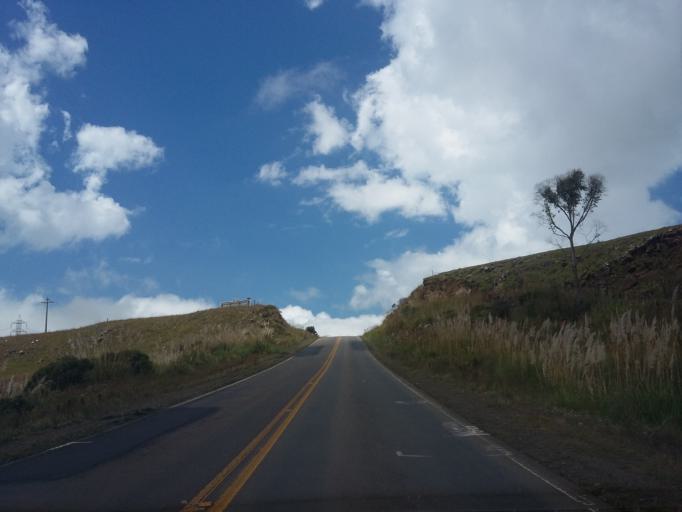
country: BR
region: Santa Catarina
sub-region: Lauro Muller
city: Lauro Muller
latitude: -28.3634
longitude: -49.5824
